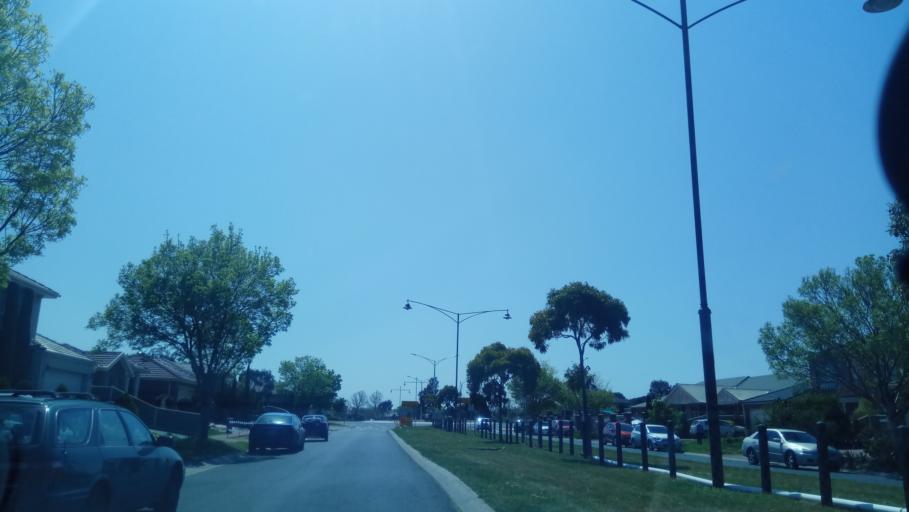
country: AU
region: Victoria
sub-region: Wyndham
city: Williams Landing
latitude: -37.8876
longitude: 144.7497
